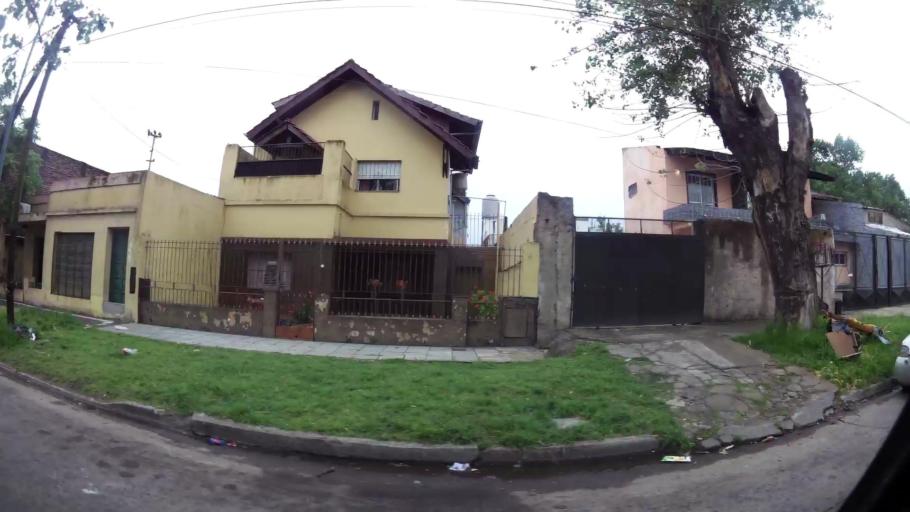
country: AR
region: Buenos Aires
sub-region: Partido de Lanus
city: Lanus
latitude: -34.7234
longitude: -58.3725
